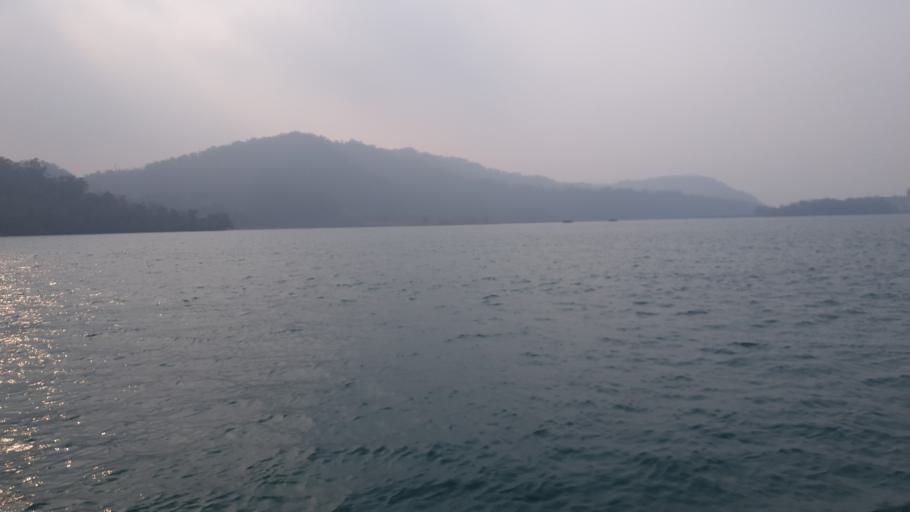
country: TW
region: Taiwan
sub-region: Nantou
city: Puli
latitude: 23.8546
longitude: 120.9116
